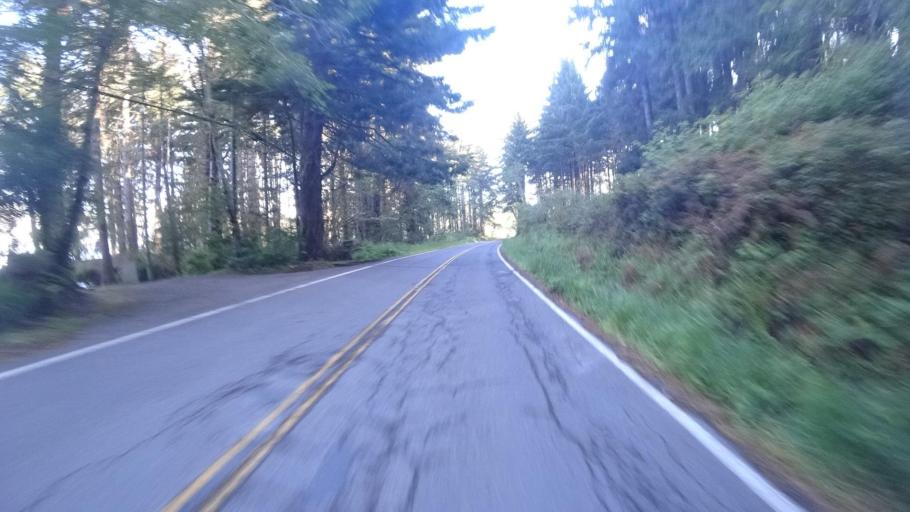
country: US
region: California
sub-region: Humboldt County
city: Westhaven-Moonstone
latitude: 41.1174
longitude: -124.1568
